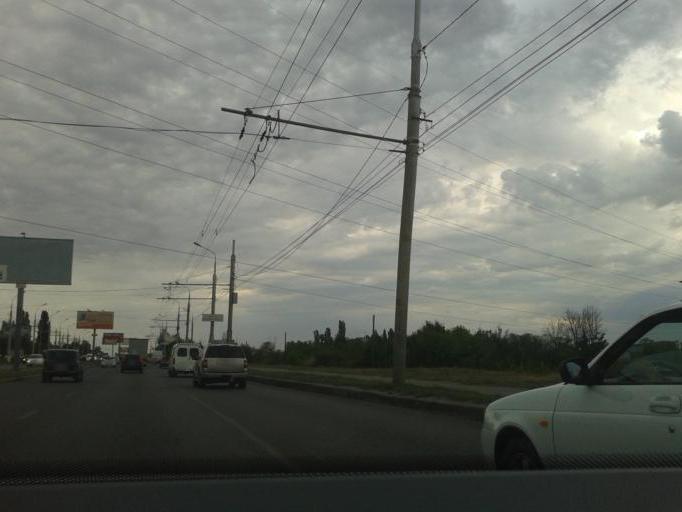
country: RU
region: Volgograd
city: Volgograd
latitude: 48.6435
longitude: 44.4328
